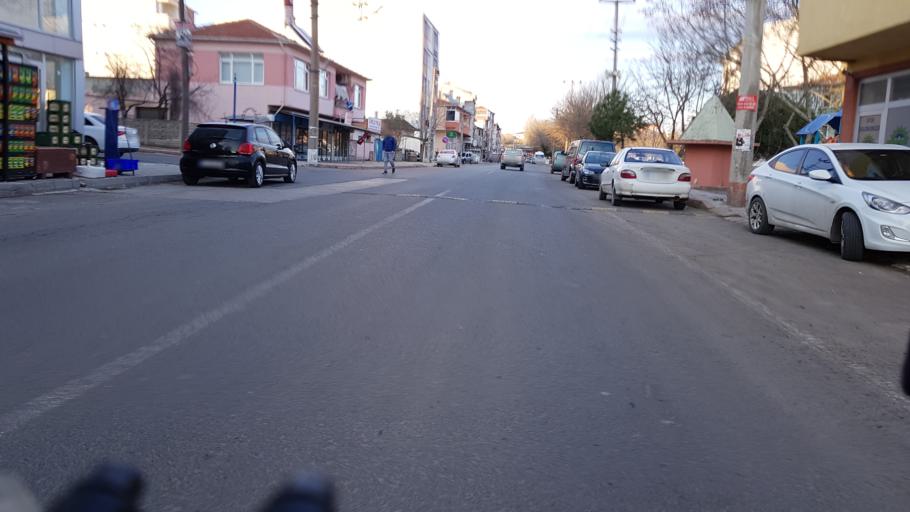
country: TR
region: Tekirdag
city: Velimese
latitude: 41.2523
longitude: 27.8758
